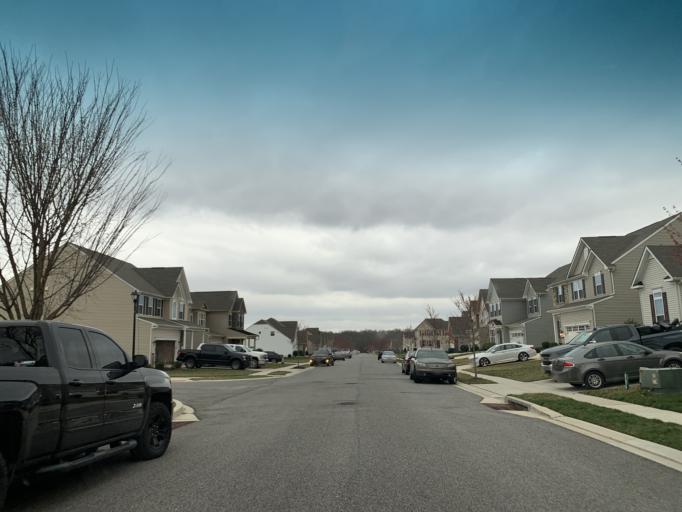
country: US
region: Maryland
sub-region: Harford County
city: Aberdeen
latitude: 39.5438
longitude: -76.1927
